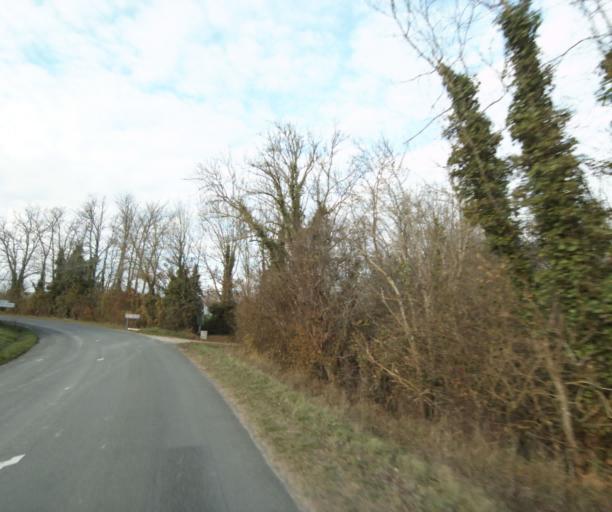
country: FR
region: Poitou-Charentes
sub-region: Departement de la Charente-Maritime
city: Les Gonds
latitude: 45.7114
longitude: -0.6030
